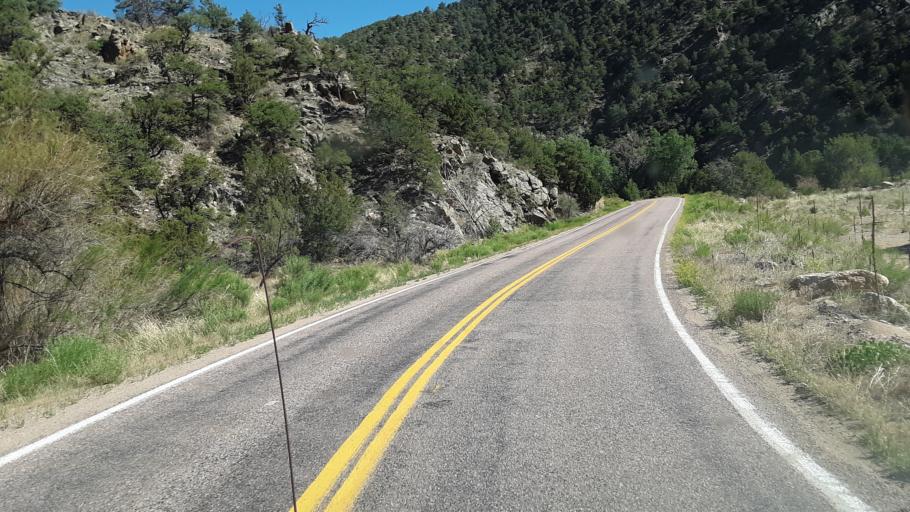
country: US
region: Colorado
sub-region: Fremont County
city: Canon City
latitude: 38.4329
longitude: -105.3923
